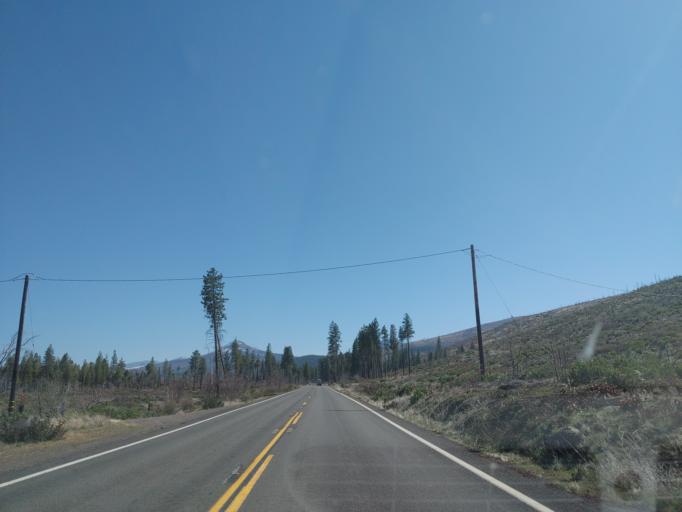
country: US
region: California
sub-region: Shasta County
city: Burney
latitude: 40.7877
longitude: -121.5059
